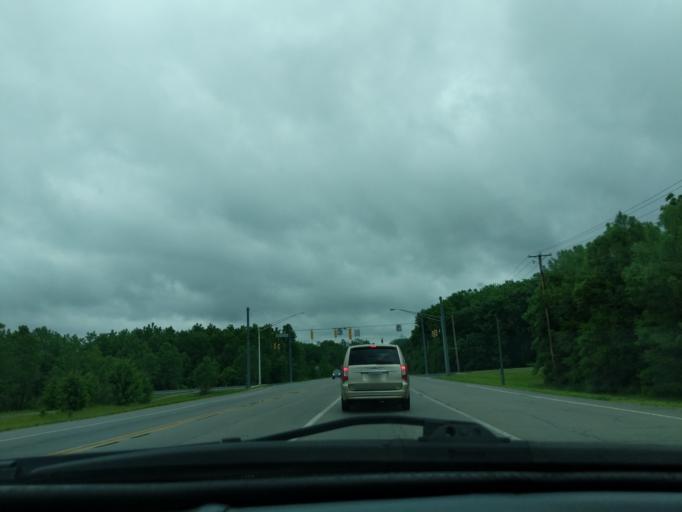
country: US
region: Indiana
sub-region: Hamilton County
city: Noblesville
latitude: 40.0553
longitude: -86.0393
